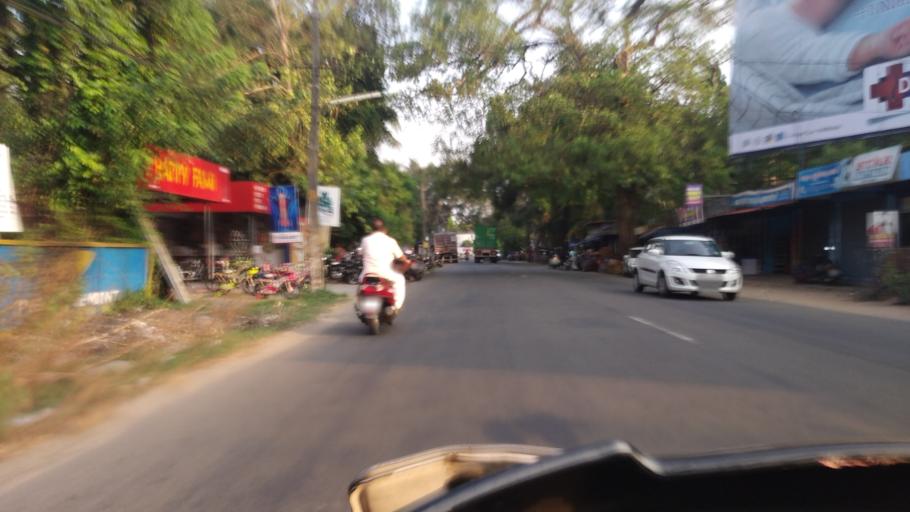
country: IN
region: Kerala
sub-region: Thrissur District
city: Irinjalakuda
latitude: 10.3329
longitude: 76.1403
